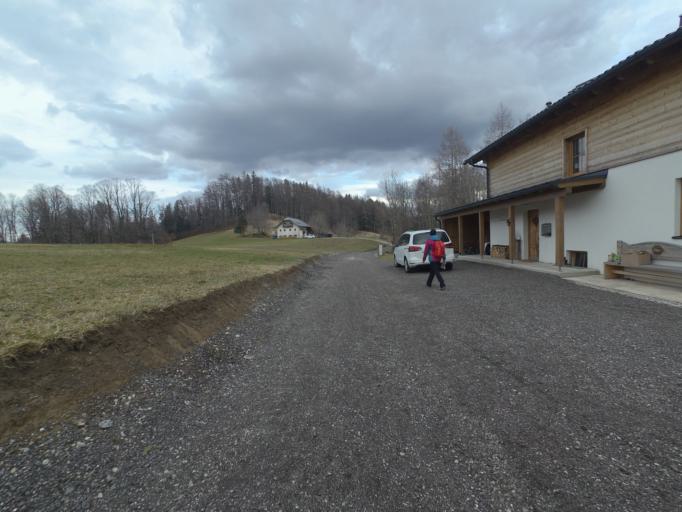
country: AT
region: Salzburg
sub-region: Politischer Bezirk Hallein
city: Hallein
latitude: 47.6652
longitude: 13.0800
